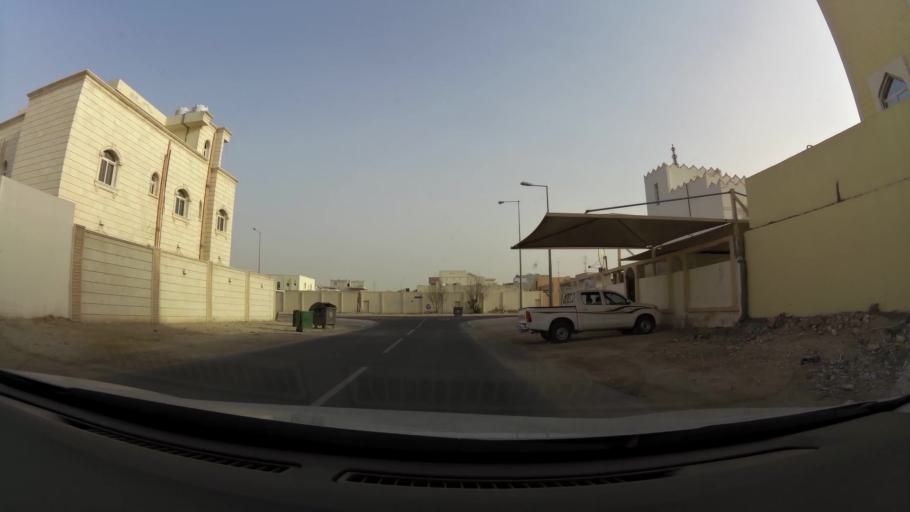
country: QA
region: Baladiyat ar Rayyan
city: Ar Rayyan
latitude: 25.2514
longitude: 51.4474
